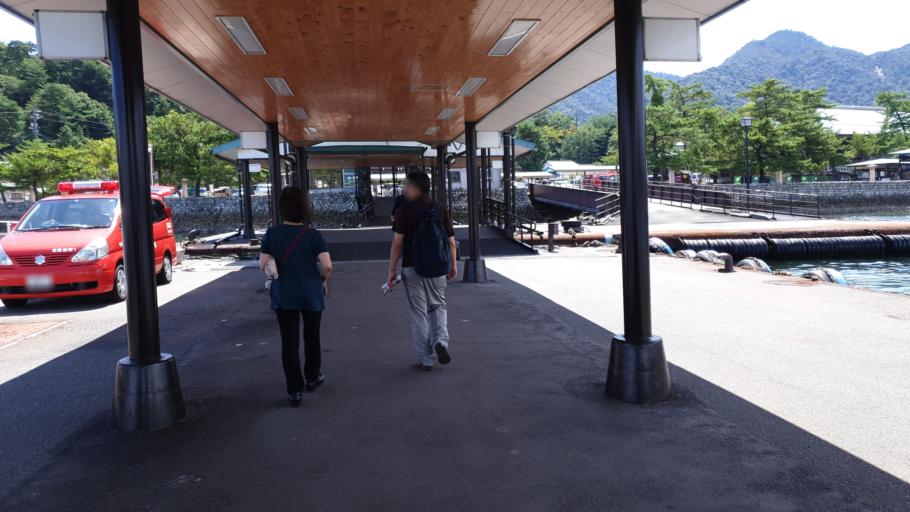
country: JP
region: Hiroshima
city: Miyajima
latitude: 34.3035
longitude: 132.3224
